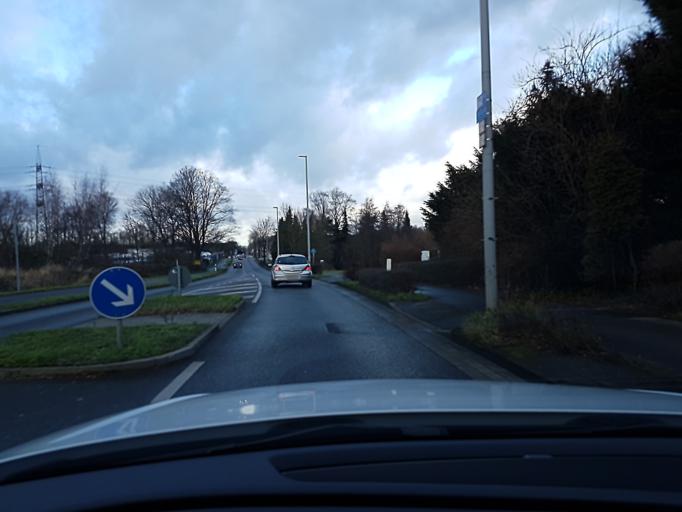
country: DE
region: North Rhine-Westphalia
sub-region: Regierungsbezirk Dusseldorf
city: Muelheim (Ruhr)
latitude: 51.3703
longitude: 6.8636
